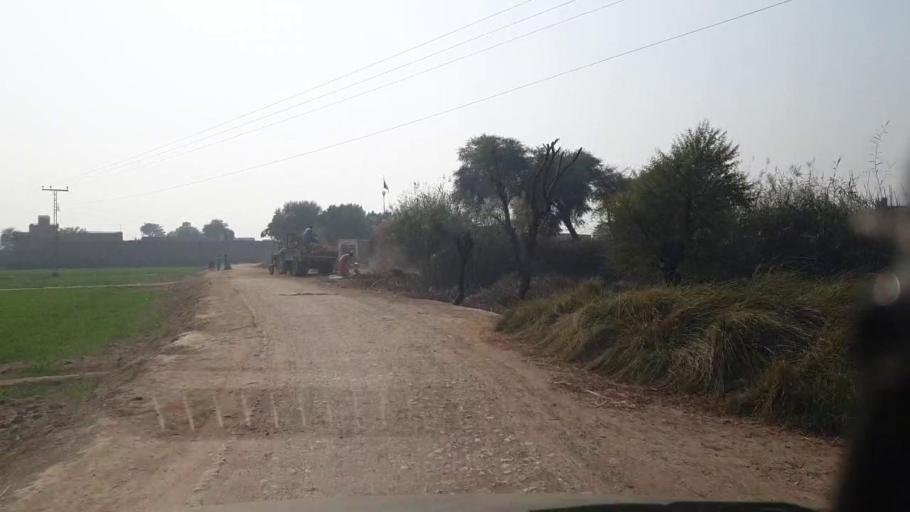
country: PK
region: Sindh
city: Shahdadpur
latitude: 26.0344
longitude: 68.5109
